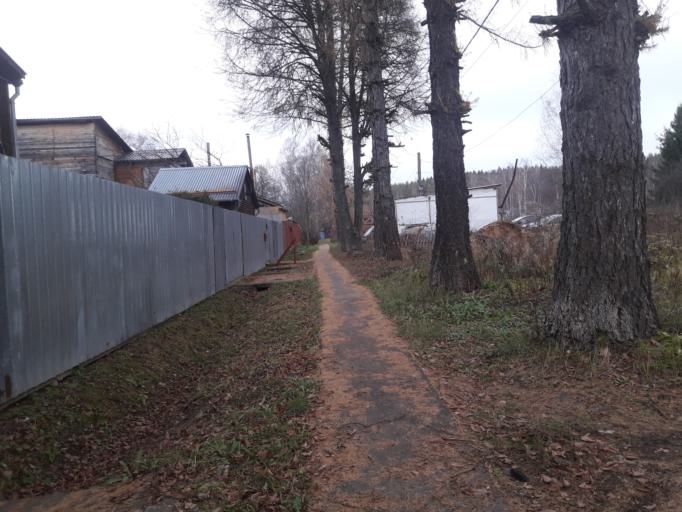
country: RU
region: Moskovskaya
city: Ashukino
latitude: 56.1669
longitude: 37.9630
